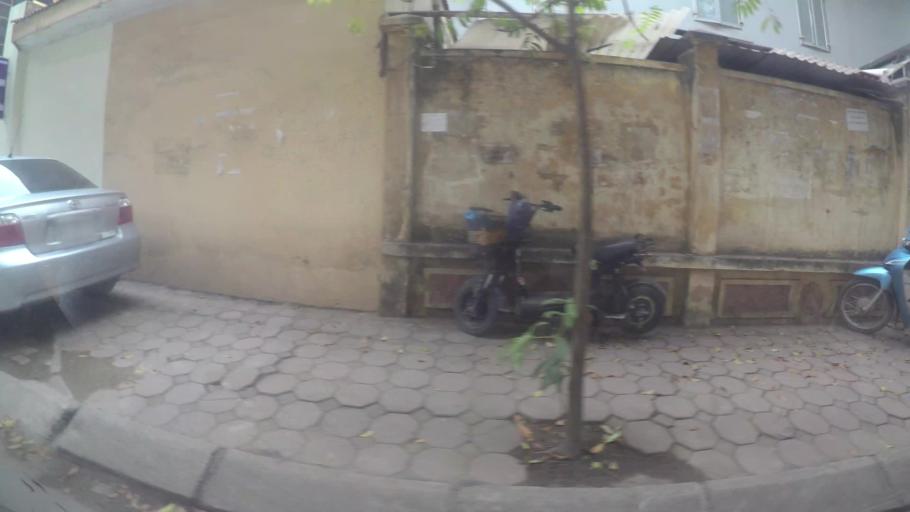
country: VN
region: Ha Noi
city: Ha Dong
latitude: 20.9704
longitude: 105.7739
